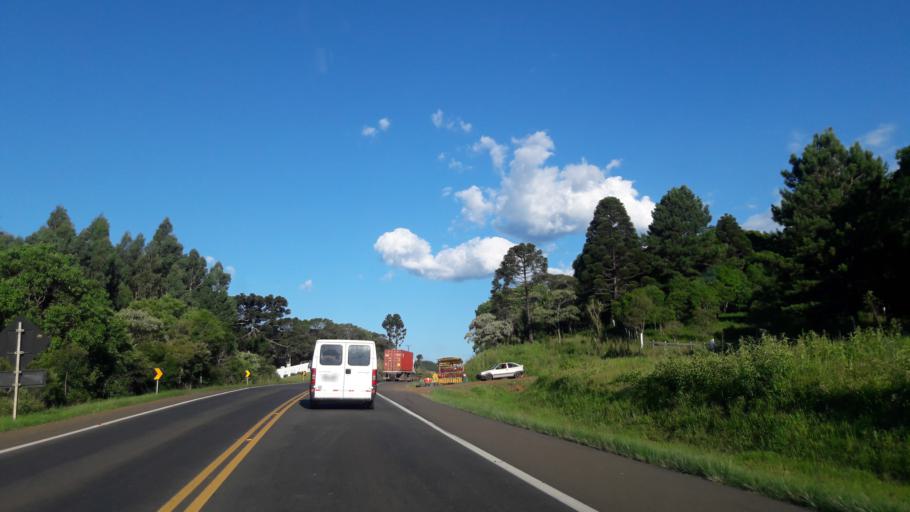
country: BR
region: Parana
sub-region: Guarapuava
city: Guarapuava
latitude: -25.3676
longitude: -51.3373
